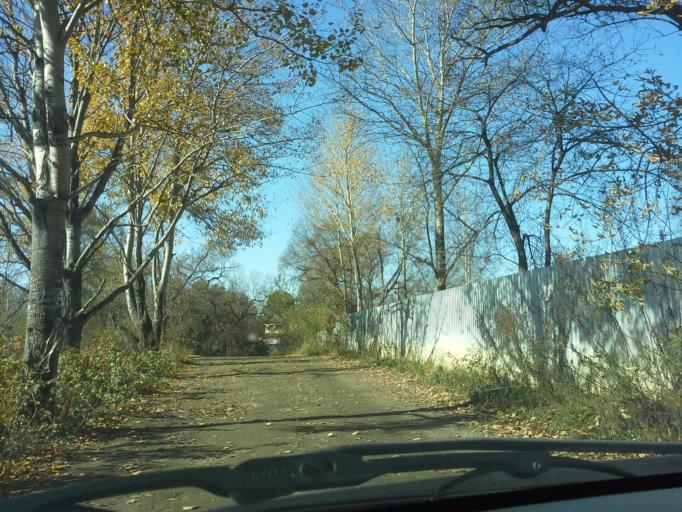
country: RU
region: Jewish Autonomous Oblast
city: Priamurskiy
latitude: 48.5318
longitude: 134.9628
